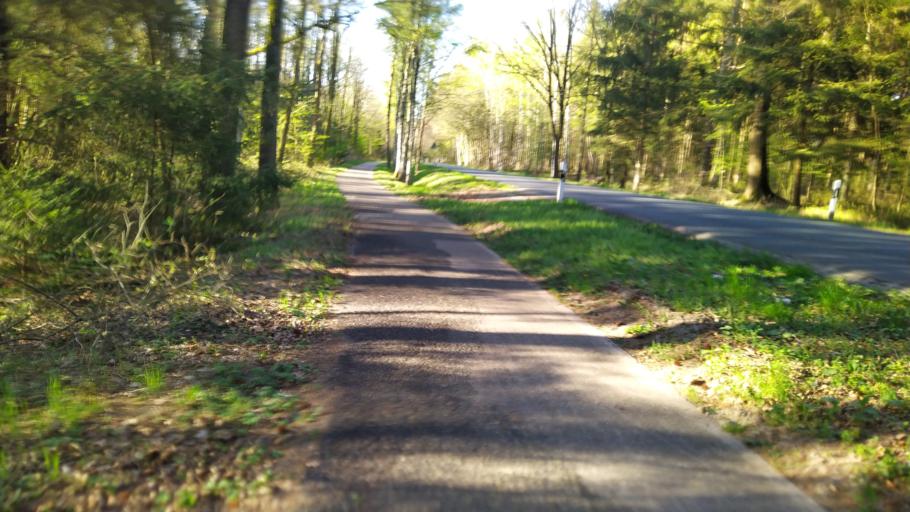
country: DE
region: Lower Saxony
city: Lengenbostel
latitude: 53.3130
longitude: 9.5058
